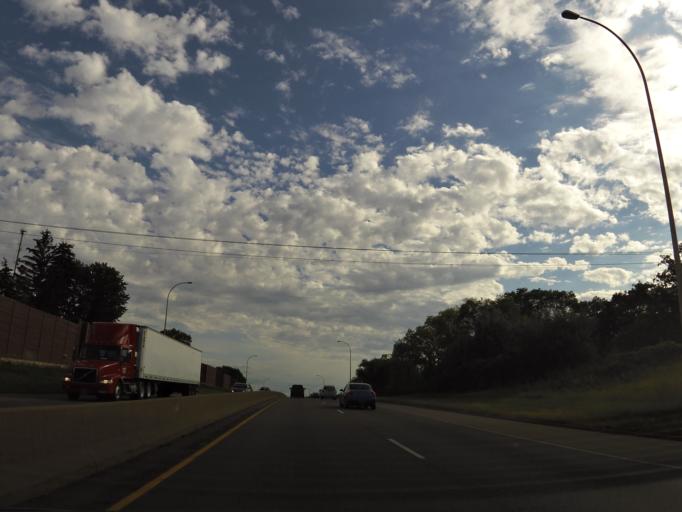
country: US
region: Minnesota
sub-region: Hennepin County
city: New Hope
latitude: 45.0024
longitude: -93.4010
